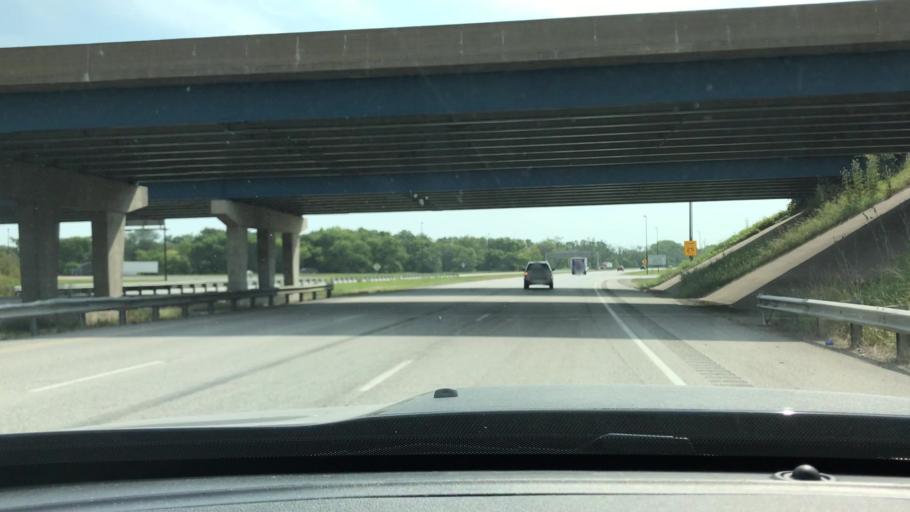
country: US
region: Illinois
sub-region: Rock Island County
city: Coal Valley
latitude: 41.4579
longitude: -90.4957
